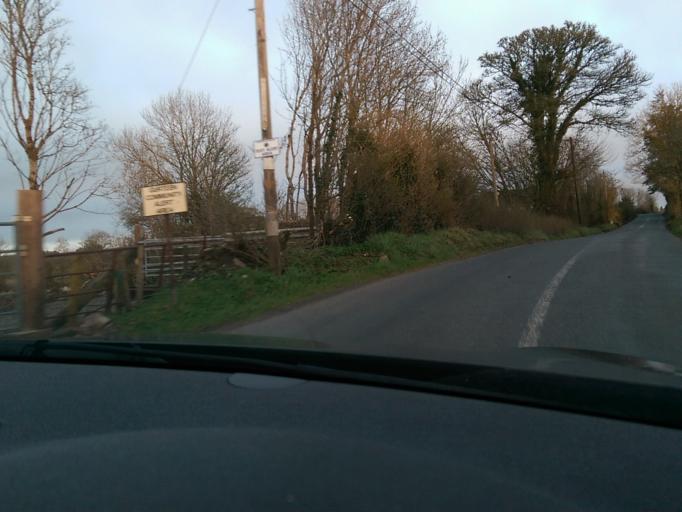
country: IE
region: Connaught
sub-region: Sligo
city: Ballymote
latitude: 54.0253
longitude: -8.5690
